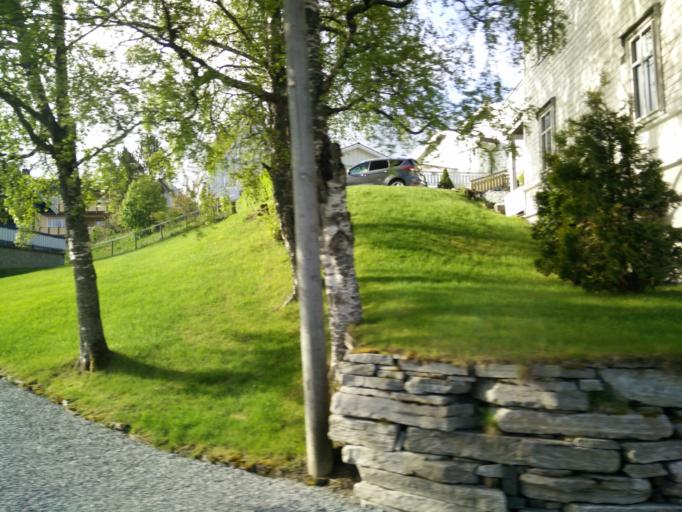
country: NO
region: Sor-Trondelag
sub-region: Skaun
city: Borsa
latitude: 63.3105
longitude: 10.1687
